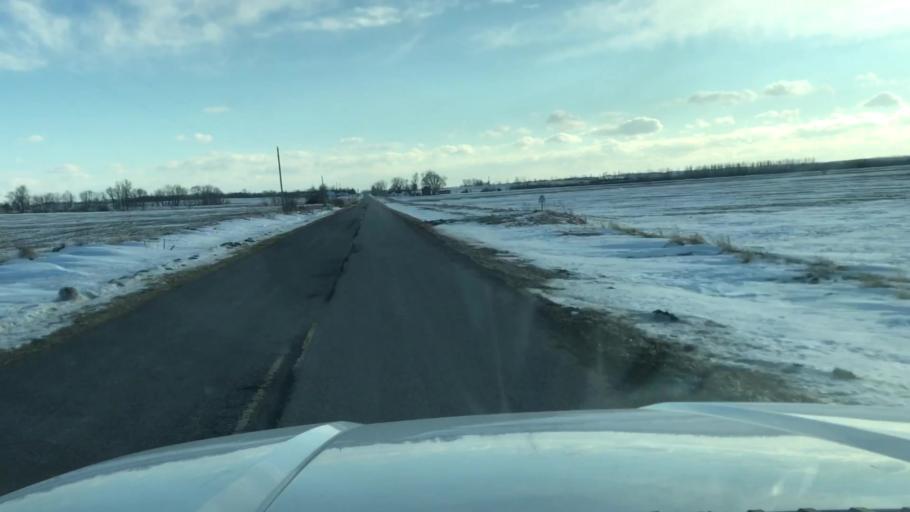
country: US
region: Missouri
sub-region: Holt County
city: Oregon
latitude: 40.1246
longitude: -95.0225
